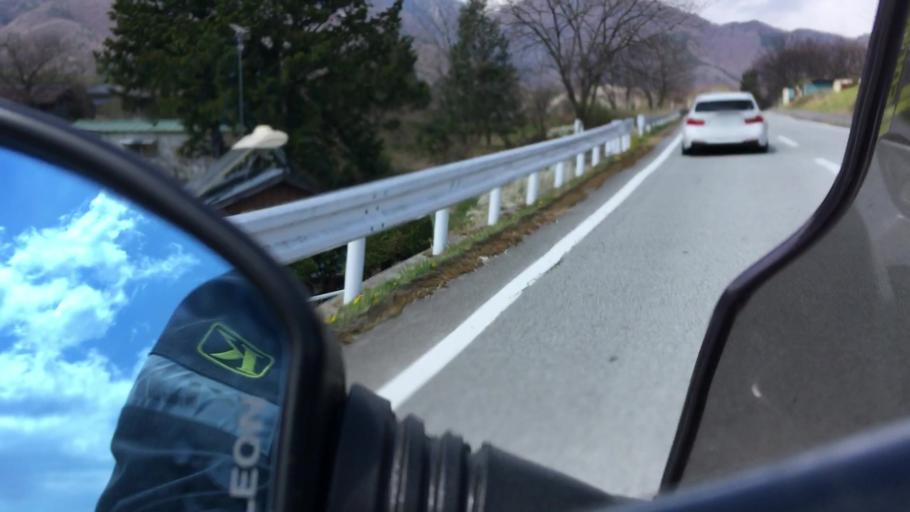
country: JP
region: Yamanashi
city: Nirasaki
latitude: 35.7820
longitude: 138.3238
